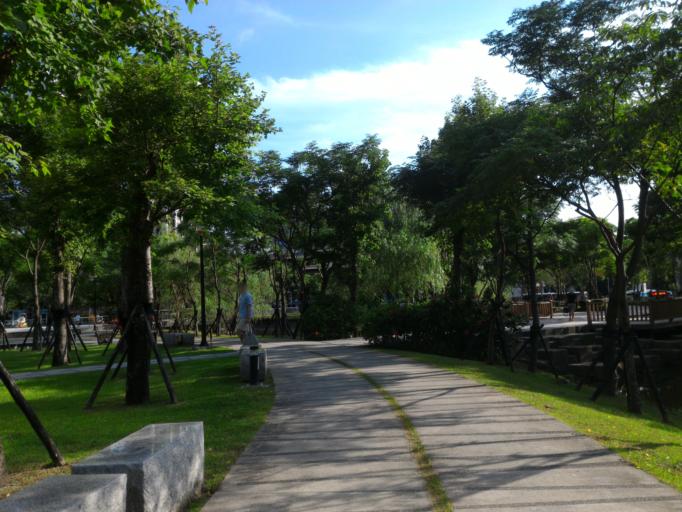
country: TW
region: Taipei
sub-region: Taipei
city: Banqiao
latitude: 25.0132
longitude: 121.4613
